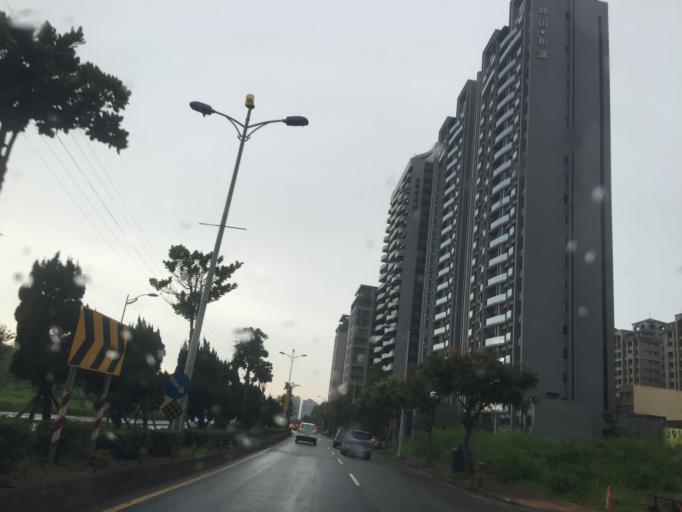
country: TW
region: Taiwan
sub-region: Hsinchu
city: Zhubei
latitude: 24.8194
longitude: 121.0089
